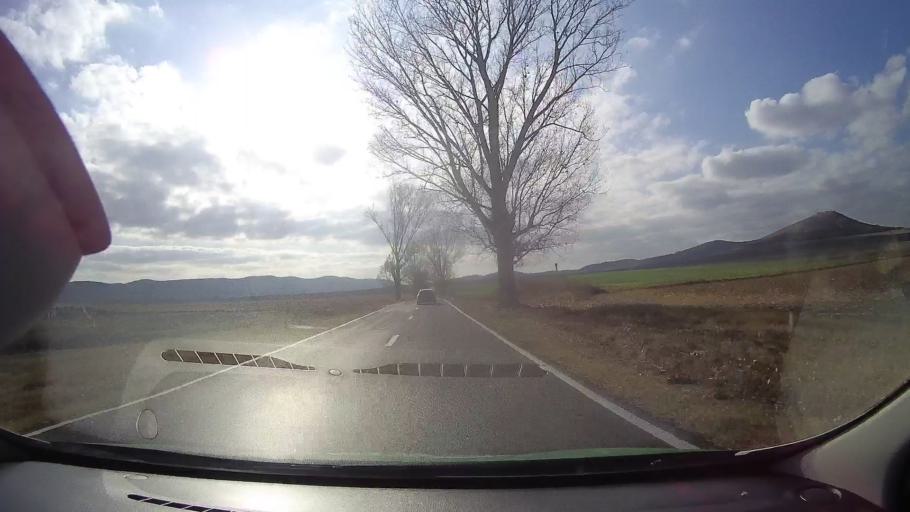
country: RO
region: Tulcea
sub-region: Comuna Nalbant
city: Nicolae Balcescu
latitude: 44.9903
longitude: 28.5614
